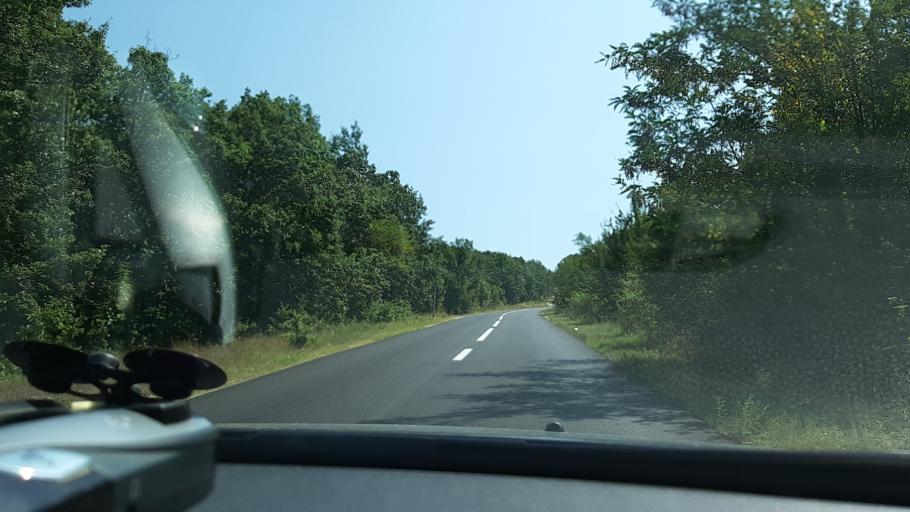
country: RO
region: Gorj
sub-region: Comuna Targu Carbunesti
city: Targu Carbunesti
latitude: 44.9475
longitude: 23.5685
